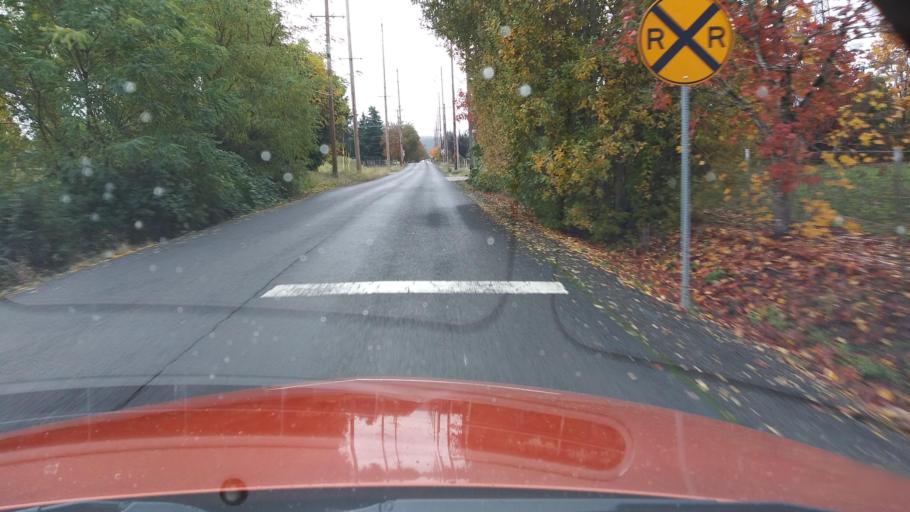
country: US
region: Oregon
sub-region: Washington County
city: Forest Grove
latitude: 45.5257
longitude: -123.0880
